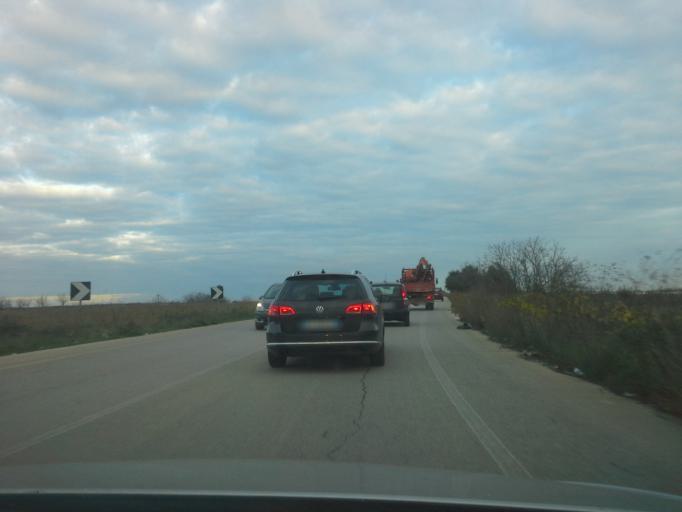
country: IT
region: Apulia
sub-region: Provincia di Bari
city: Adelfia
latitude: 41.0088
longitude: 16.8545
